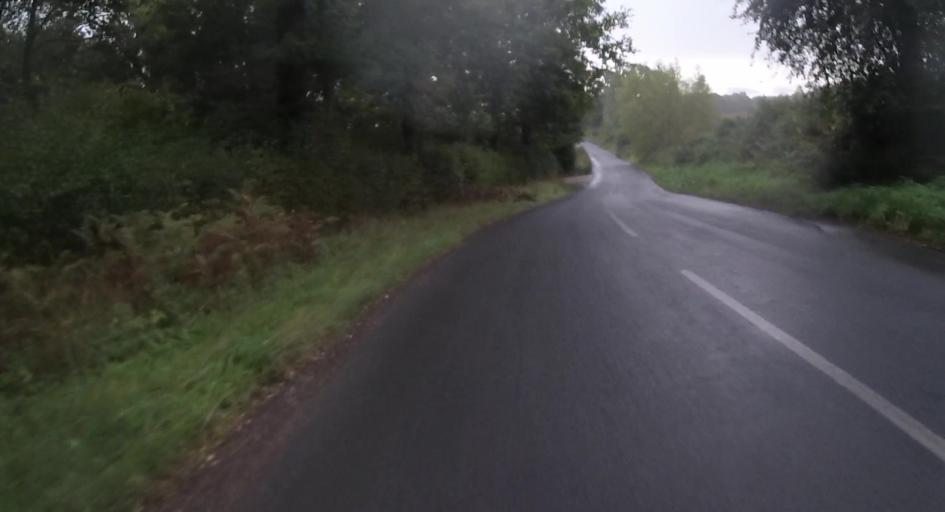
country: GB
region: England
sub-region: Hampshire
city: Tadley
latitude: 51.3128
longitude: -1.1418
